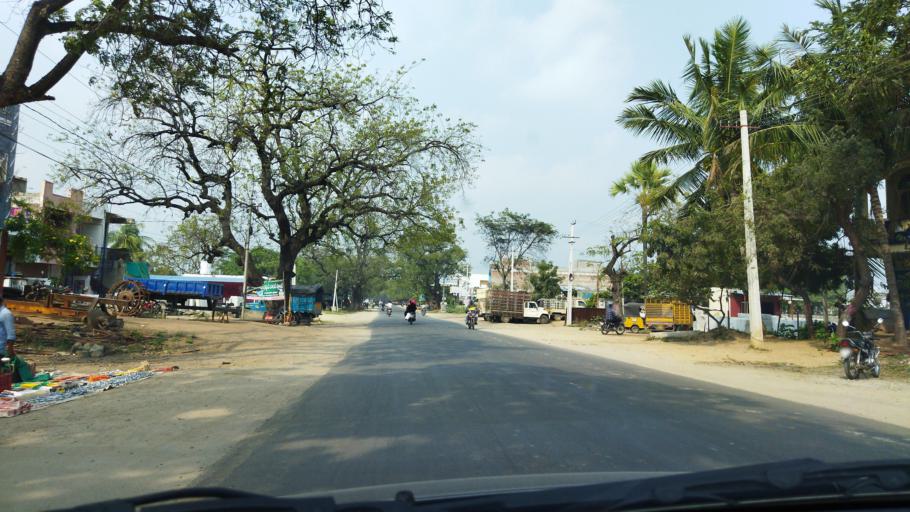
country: IN
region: Telangana
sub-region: Nalgonda
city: Nalgonda
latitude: 17.1666
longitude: 79.4193
